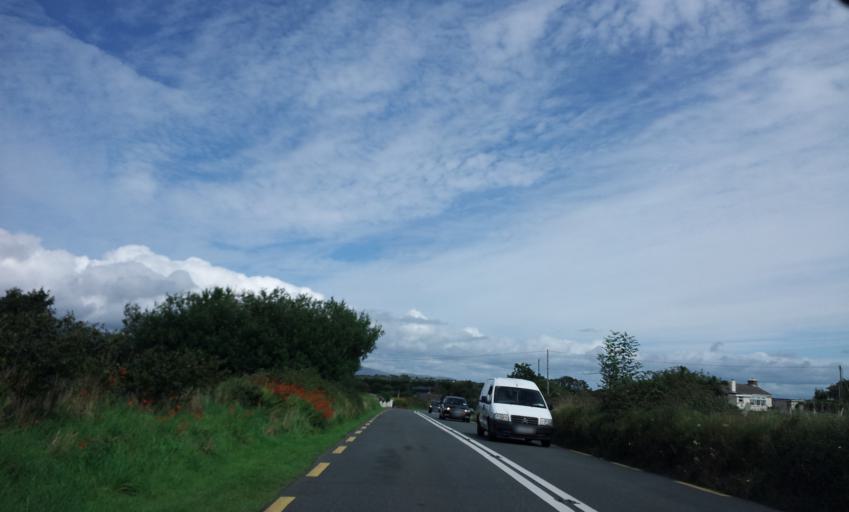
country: IE
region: Munster
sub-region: Ciarrai
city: Killorglin
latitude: 52.0915
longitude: -9.8466
